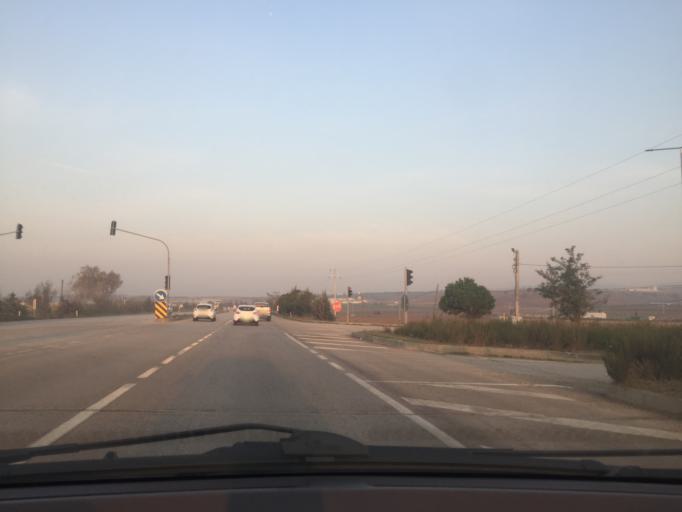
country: TR
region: Bursa
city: Karacabey
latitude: 40.2360
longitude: 28.3150
